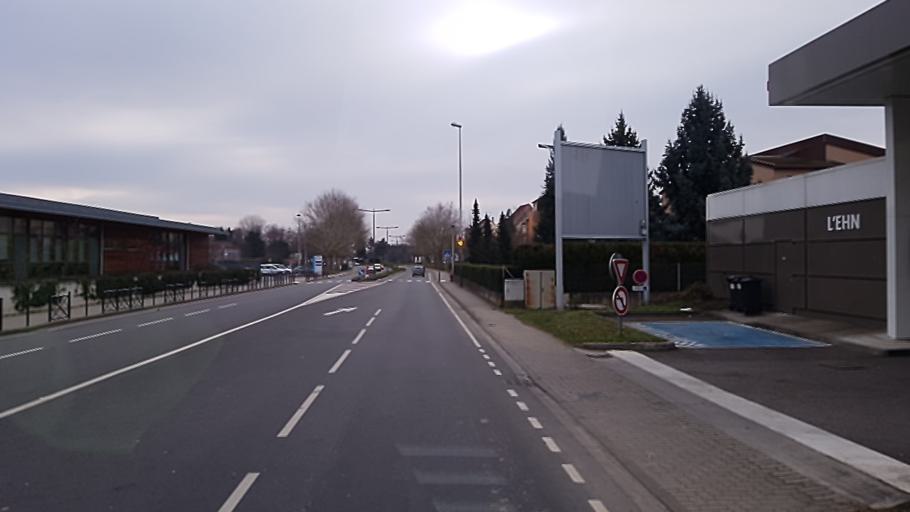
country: FR
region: Alsace
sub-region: Departement du Bas-Rhin
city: Obernai
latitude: 48.4598
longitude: 7.4949
